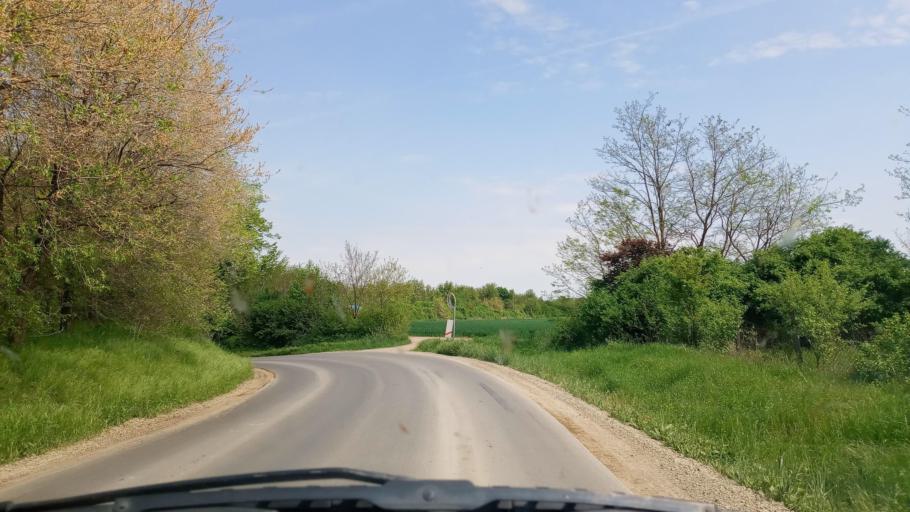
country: HU
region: Baranya
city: Boly
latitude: 45.9401
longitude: 18.5426
